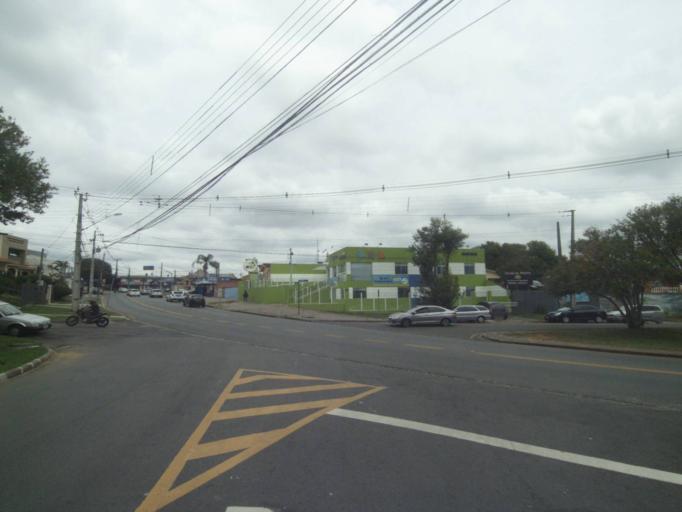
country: BR
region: Parana
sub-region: Curitiba
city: Curitiba
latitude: -25.3952
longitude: -49.2882
